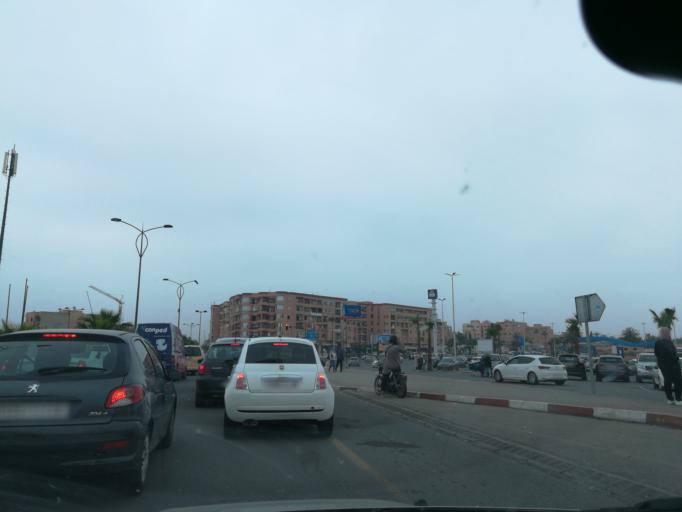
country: MA
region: Marrakech-Tensift-Al Haouz
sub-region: Marrakech
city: Marrakesh
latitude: 31.6682
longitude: -8.0119
